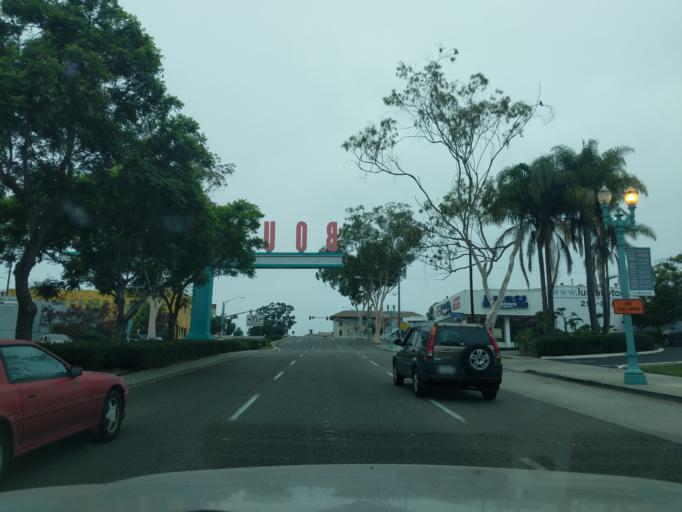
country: US
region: California
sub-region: San Diego County
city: San Diego
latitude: 32.7554
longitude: -117.1445
